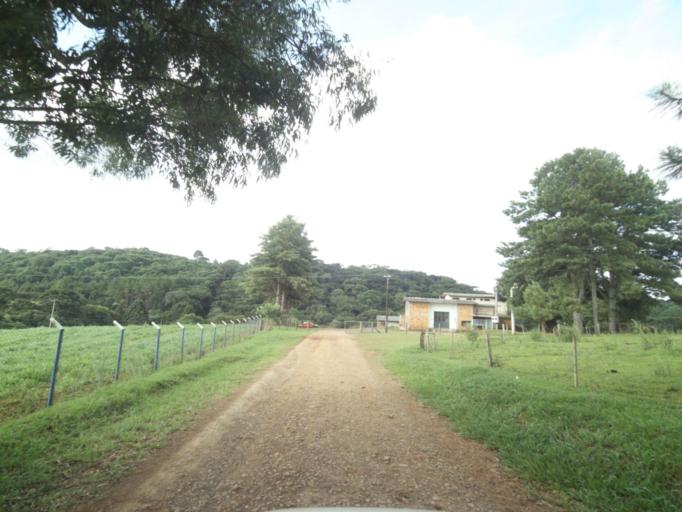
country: BR
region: Rio Grande do Sul
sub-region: Lagoa Vermelha
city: Lagoa Vermelha
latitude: -28.2037
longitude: -51.5419
